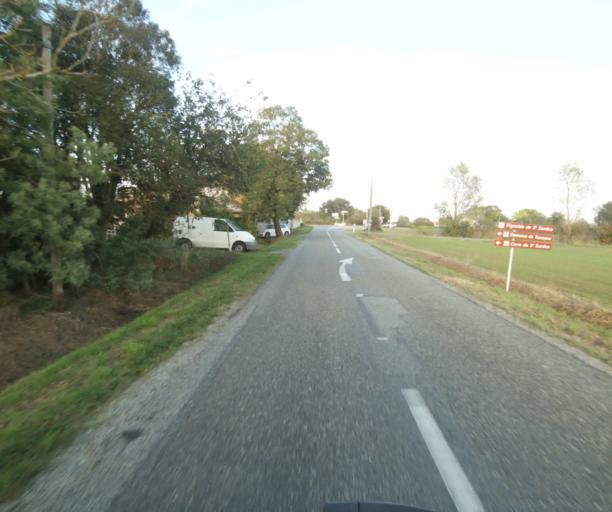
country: FR
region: Midi-Pyrenees
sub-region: Departement du Tarn-et-Garonne
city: Verdun-sur-Garonne
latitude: 43.8335
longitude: 1.1587
